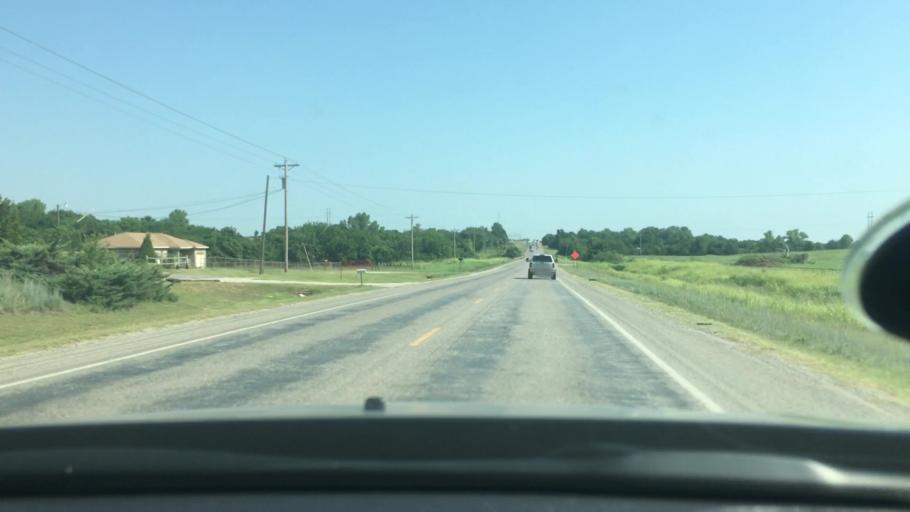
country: US
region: Oklahoma
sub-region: Garvin County
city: Lindsay
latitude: 34.7860
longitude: -97.5983
